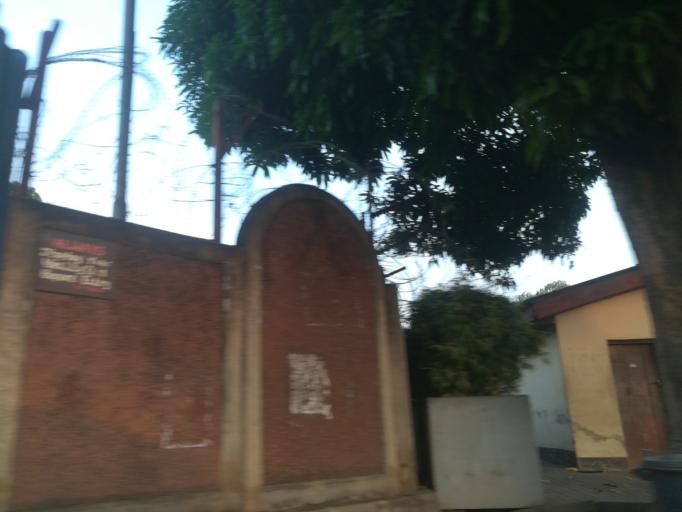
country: NG
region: Abuja Federal Capital Territory
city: Abuja
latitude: 9.0784
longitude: 7.3920
